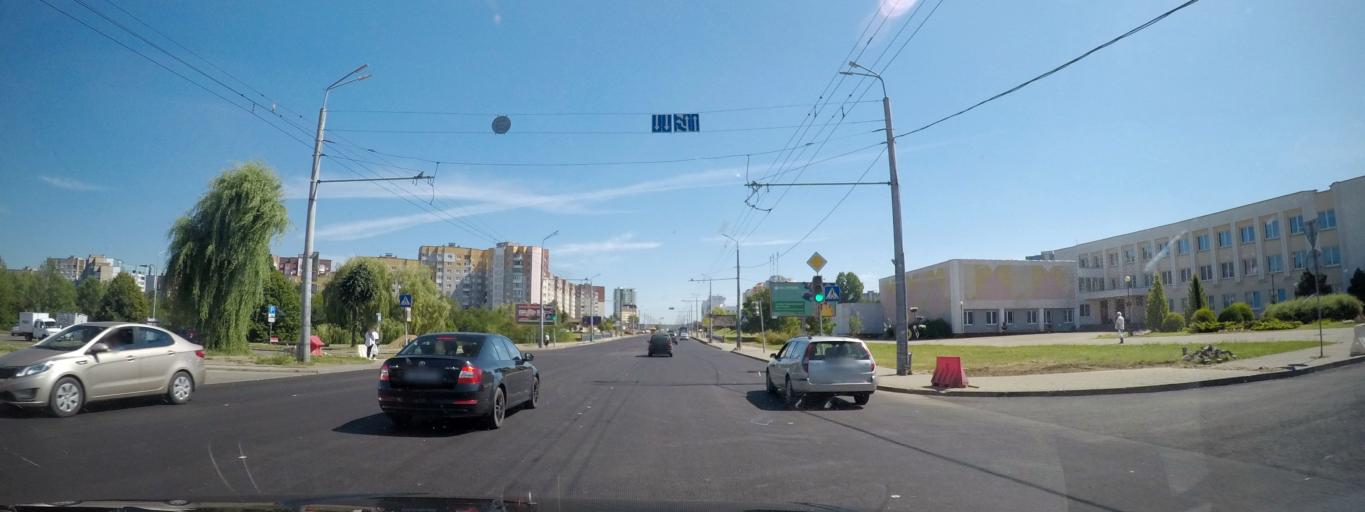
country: BY
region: Grodnenskaya
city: Hrodna
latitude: 53.6570
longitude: 23.8420
